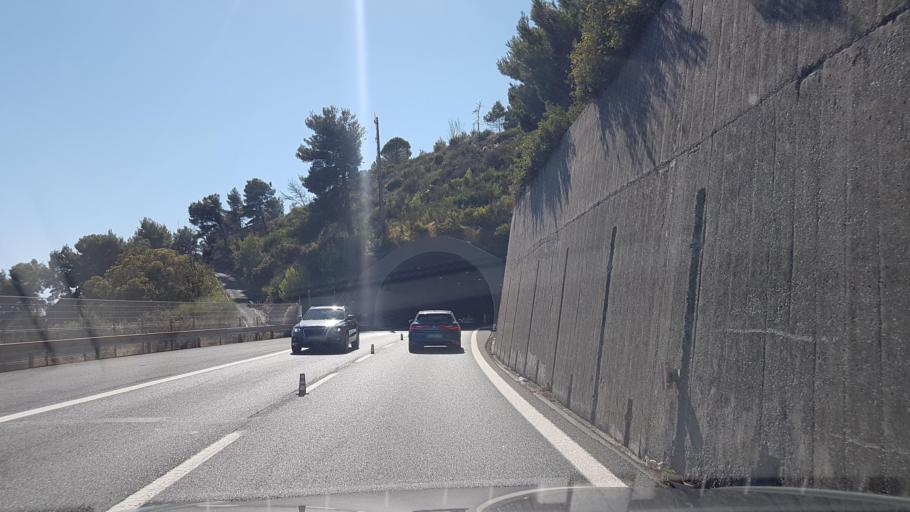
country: IT
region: Liguria
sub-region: Provincia di Imperia
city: Bordighera
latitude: 43.7941
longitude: 7.6879
